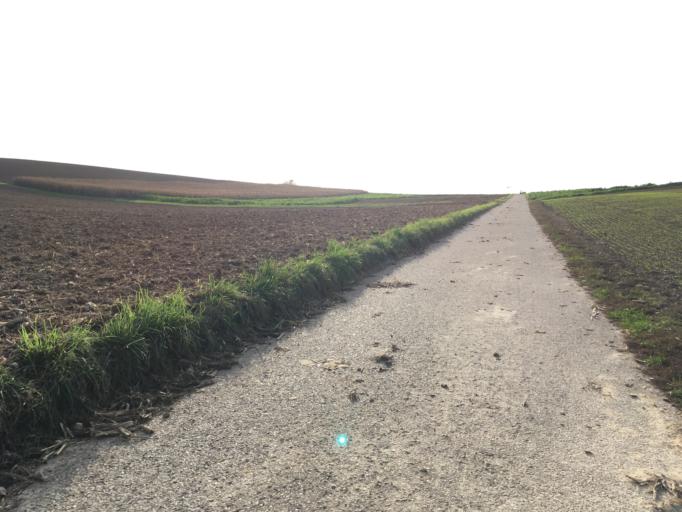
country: DE
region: Baden-Wuerttemberg
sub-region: Karlsruhe Region
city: Balzfeld
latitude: 49.2704
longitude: 8.8138
